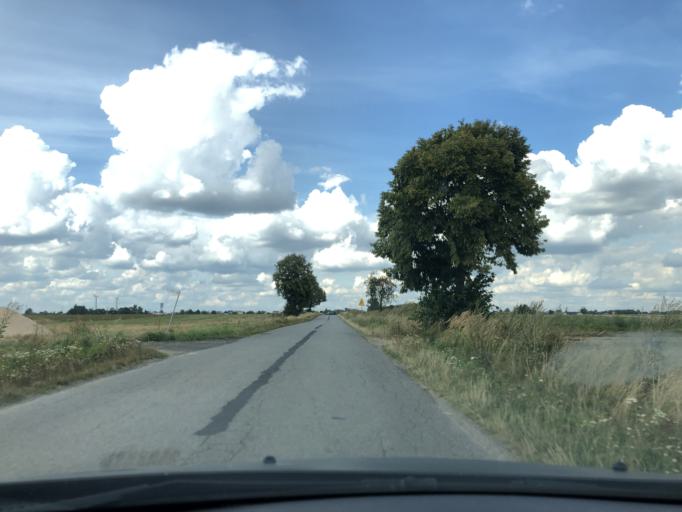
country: PL
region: Lodz Voivodeship
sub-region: Powiat wieruszowski
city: Walichnowy
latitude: 51.2513
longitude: 18.3899
